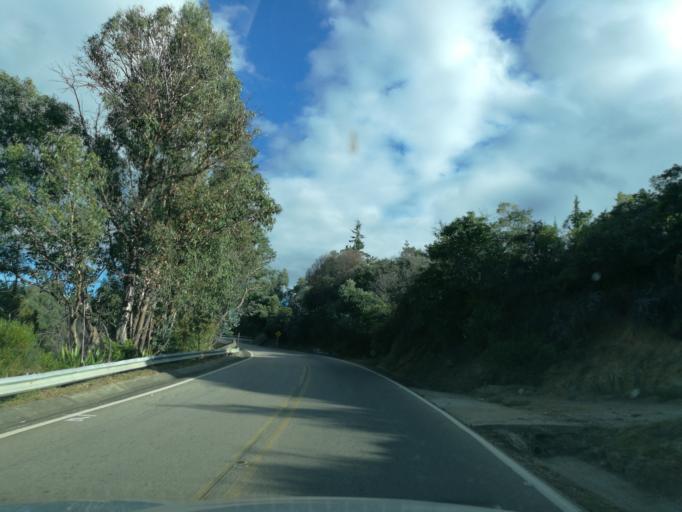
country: CO
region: Boyaca
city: Raquira
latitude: 5.5703
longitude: -73.6811
